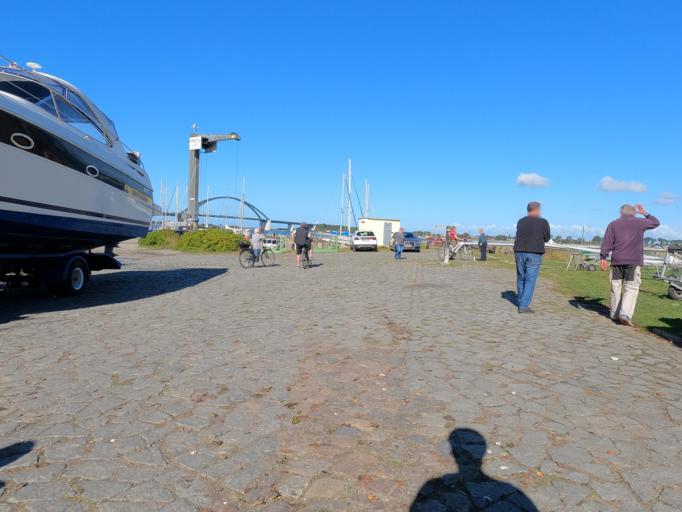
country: DE
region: Schleswig-Holstein
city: Grossenbrode
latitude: 54.3933
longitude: 11.1185
